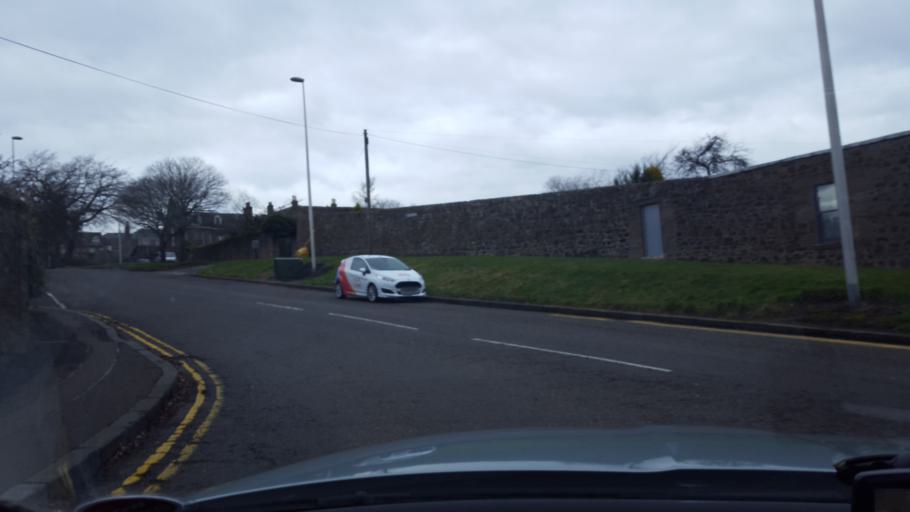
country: GB
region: Scotland
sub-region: Dundee City
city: Dundee
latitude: 56.4666
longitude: -2.9810
